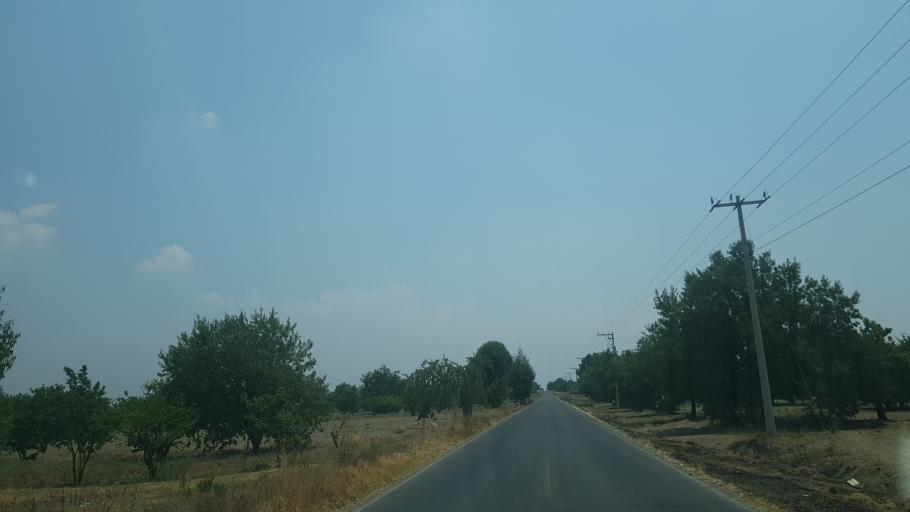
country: MX
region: Puebla
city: San Andres Calpan
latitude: 19.0988
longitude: -98.4283
